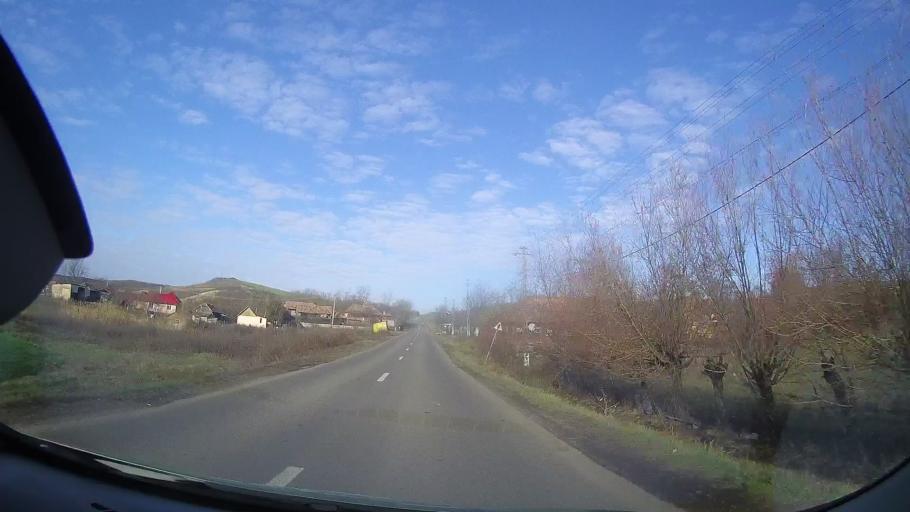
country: RO
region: Mures
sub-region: Comuna Saulia
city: Saulia
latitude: 46.6128
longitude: 24.2564
